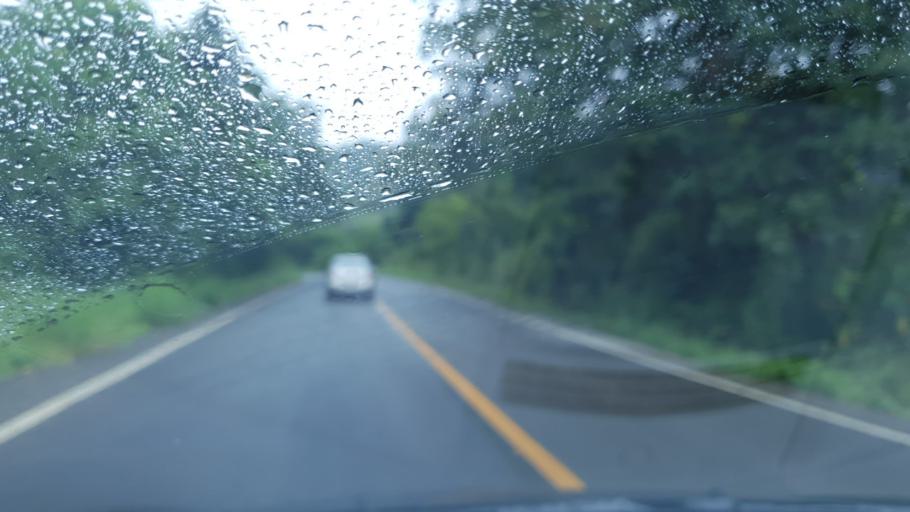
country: TH
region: Mae Hong Son
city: Khun Yuam
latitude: 18.6889
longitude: 97.9203
